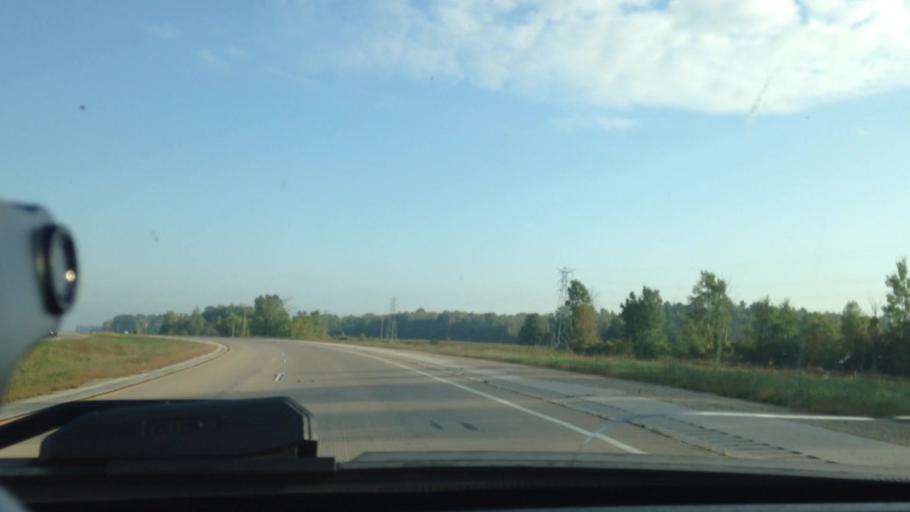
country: US
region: Wisconsin
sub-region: Oconto County
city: Oconto Falls
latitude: 44.9917
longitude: -88.0455
